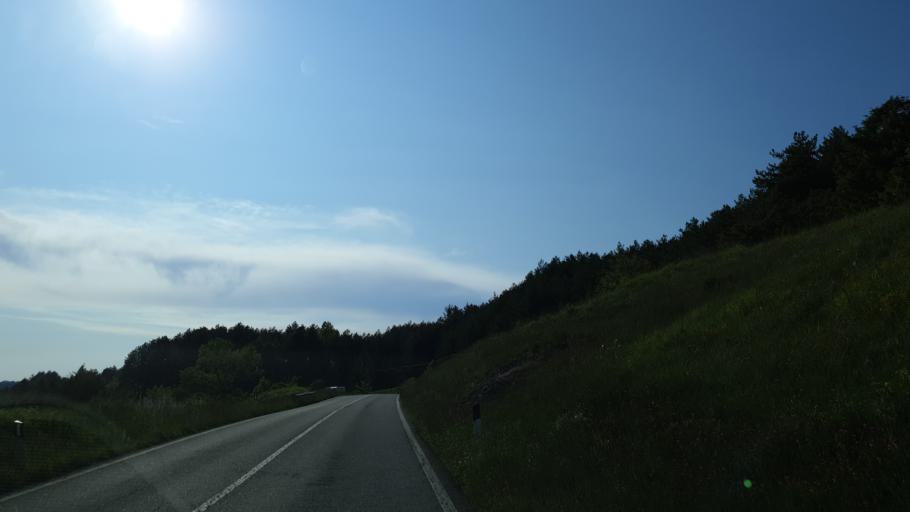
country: IT
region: Tuscany
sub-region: Province of Arezzo
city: Montemignaio
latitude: 43.7869
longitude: 11.6467
